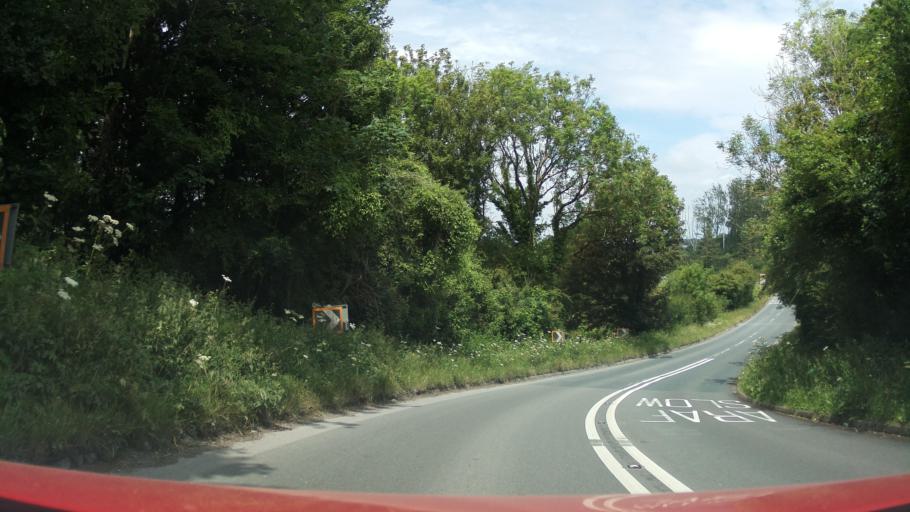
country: GB
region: Wales
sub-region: Vale of Glamorgan
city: Rhoose
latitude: 51.3991
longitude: -3.3898
